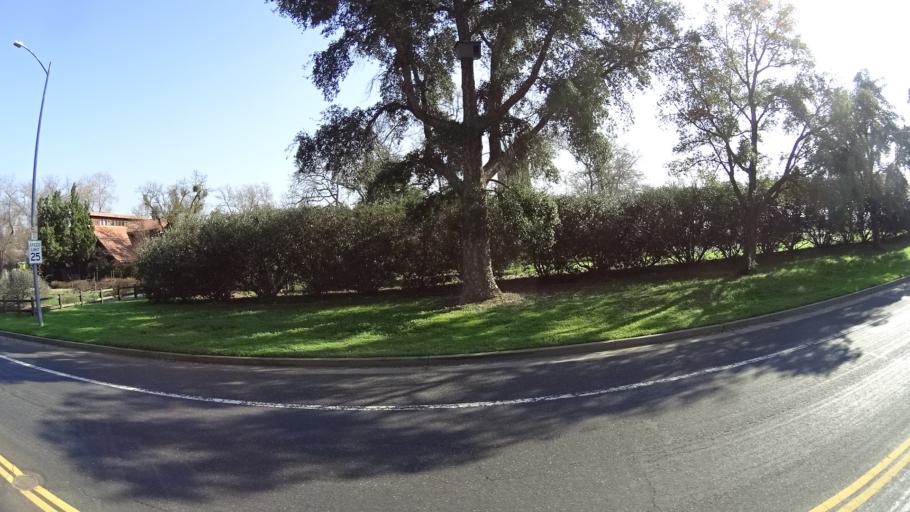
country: US
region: California
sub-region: Yolo County
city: Davis
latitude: 38.5471
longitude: -121.7818
